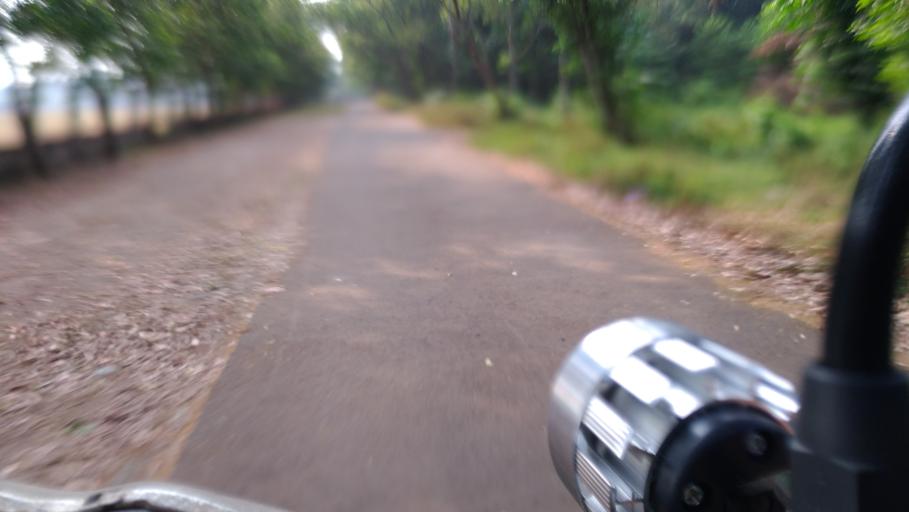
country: ID
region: West Java
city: Cileungsir
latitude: -6.3570
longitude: 106.9031
